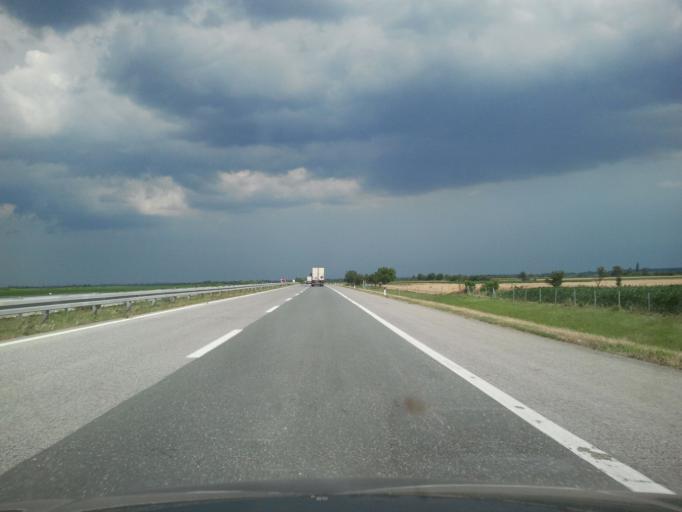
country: RS
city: Ravnje
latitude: 45.0250
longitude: 19.4831
